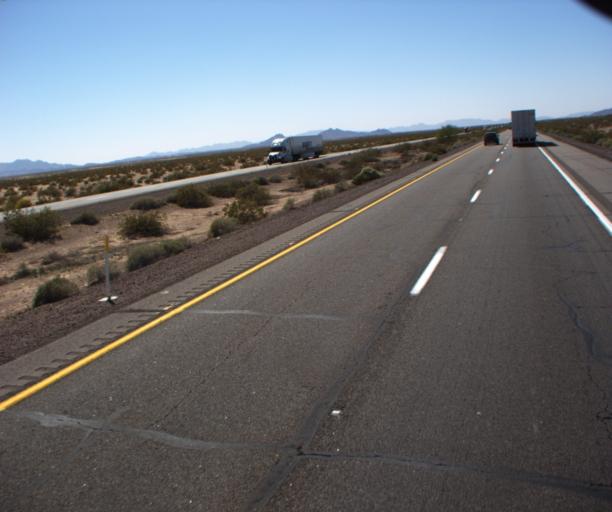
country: US
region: Arizona
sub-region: Yuma County
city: Wellton
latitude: 32.7106
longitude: -113.8424
